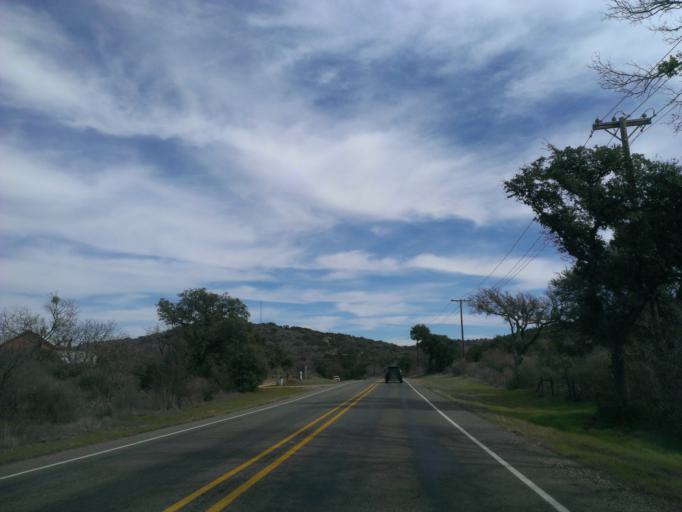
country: US
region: Texas
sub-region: Llano County
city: Kingsland
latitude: 30.6718
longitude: -98.3966
